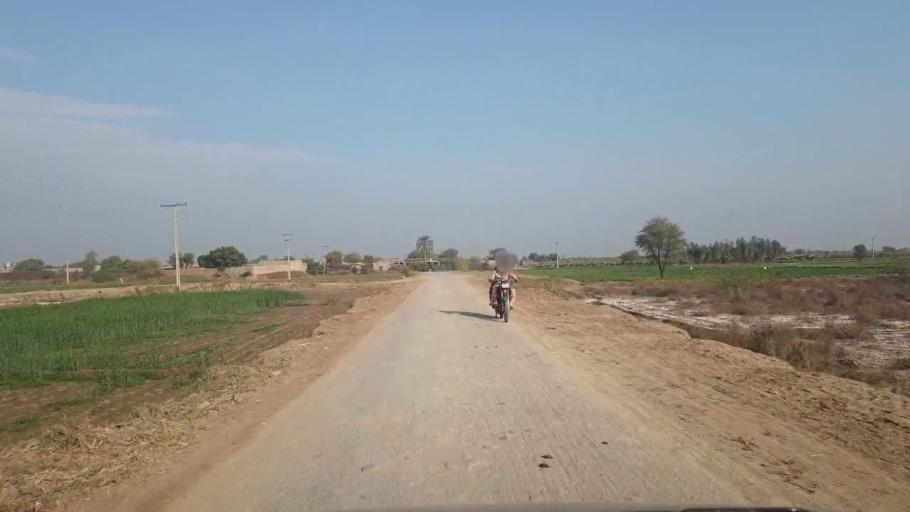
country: PK
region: Sindh
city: Tando Adam
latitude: 25.7447
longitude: 68.6069
